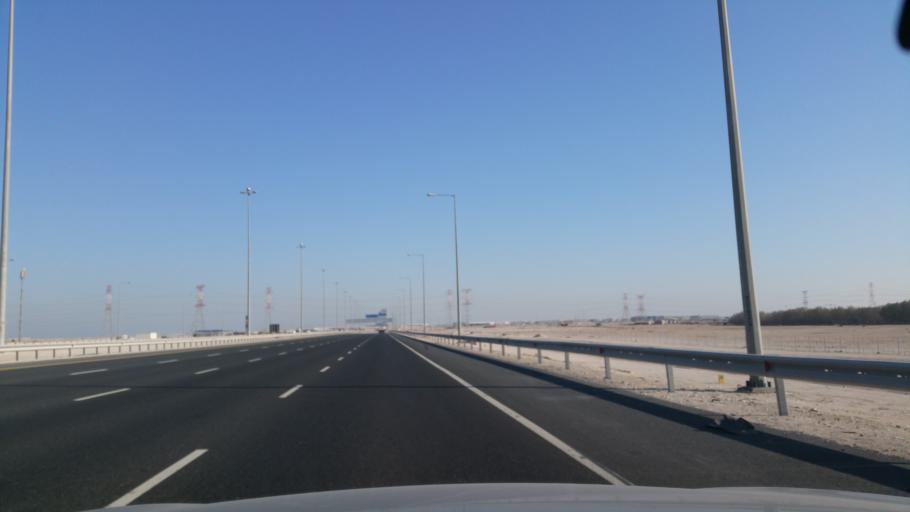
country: QA
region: Al Wakrah
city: Al Wukayr
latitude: 25.1087
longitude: 51.5011
